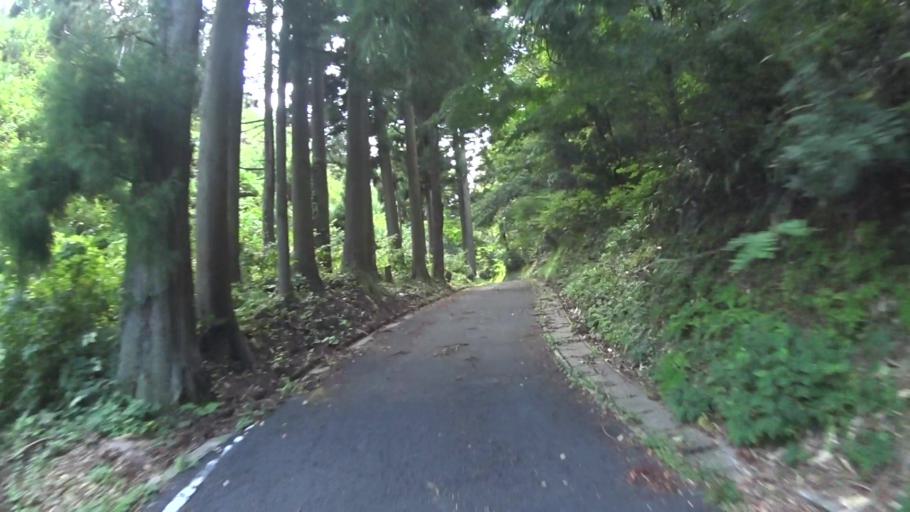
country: JP
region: Kyoto
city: Miyazu
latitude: 35.6669
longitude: 135.1364
